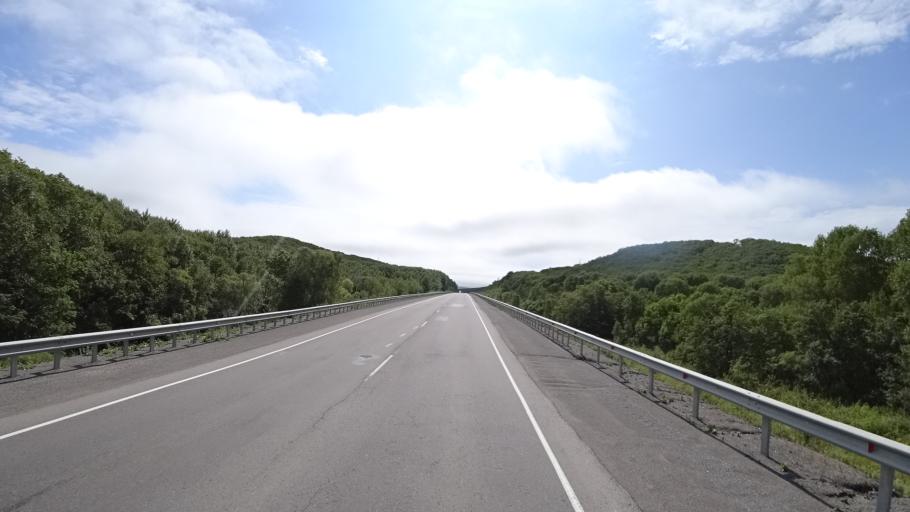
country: RU
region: Primorskiy
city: Lyalichi
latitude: 44.1269
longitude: 132.4247
